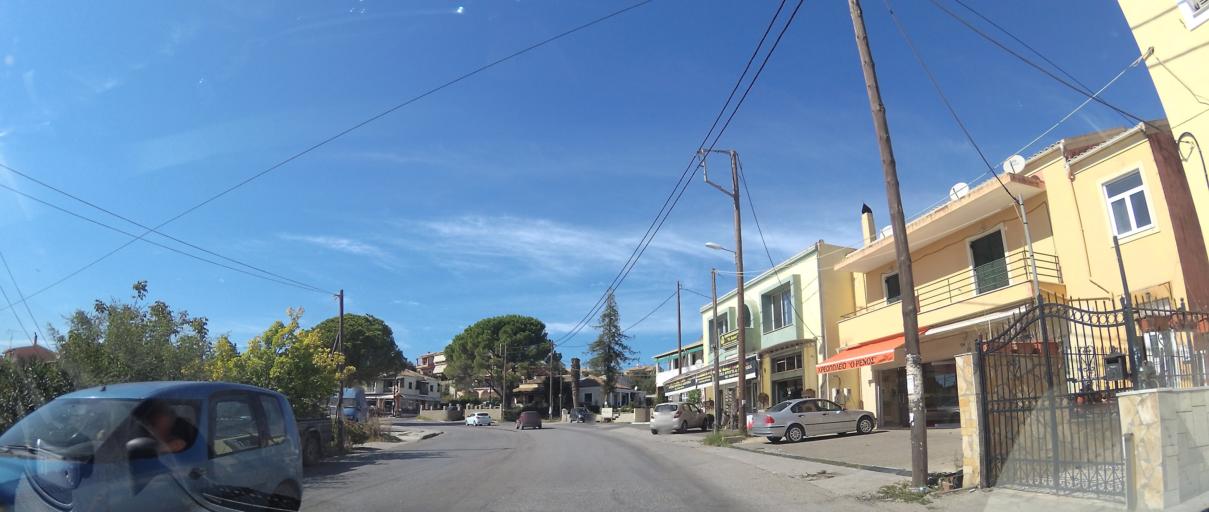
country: GR
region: Ionian Islands
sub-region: Nomos Kerkyras
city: Alepou
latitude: 39.6171
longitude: 19.8997
